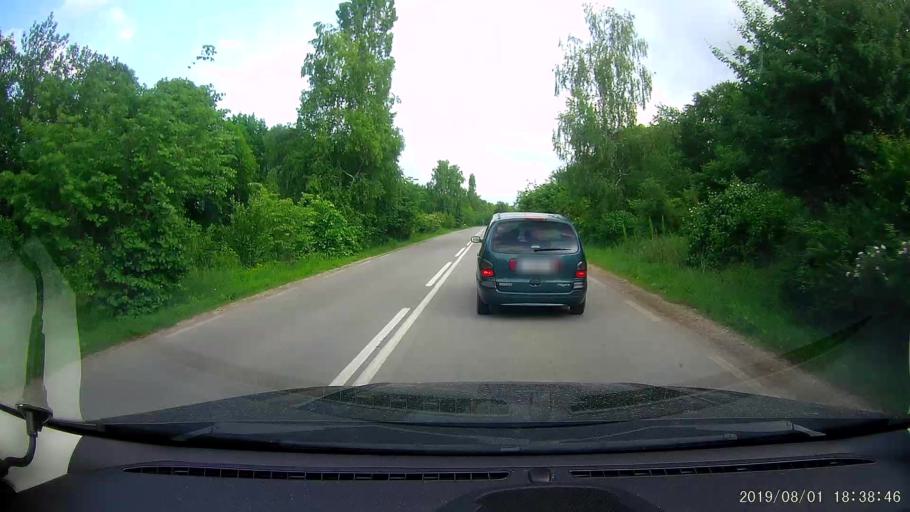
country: BG
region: Shumen
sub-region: Obshtina Khitrino
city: Gara Khitrino
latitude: 43.3979
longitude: 26.9165
